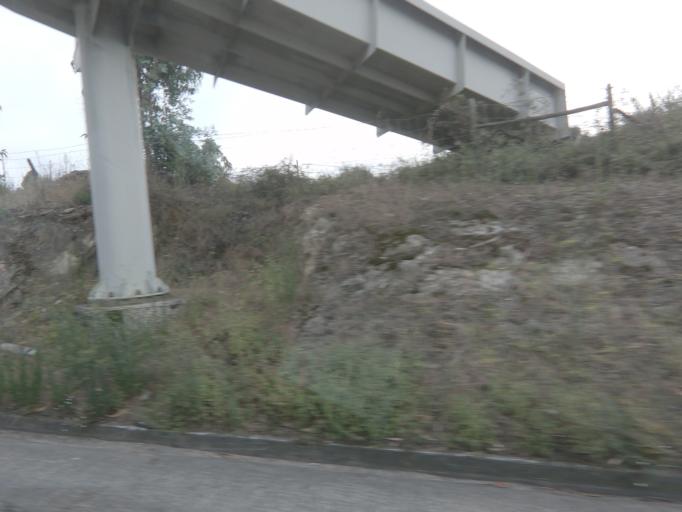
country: PT
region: Aveiro
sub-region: Mealhada
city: Pampilhosa do Botao
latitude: 40.3082
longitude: -8.3728
